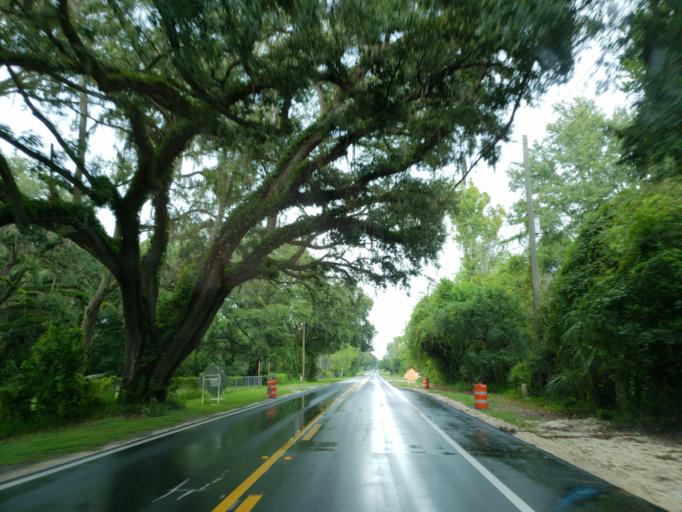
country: US
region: Florida
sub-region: Pasco County
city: Land O' Lakes
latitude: 28.2850
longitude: -82.4358
